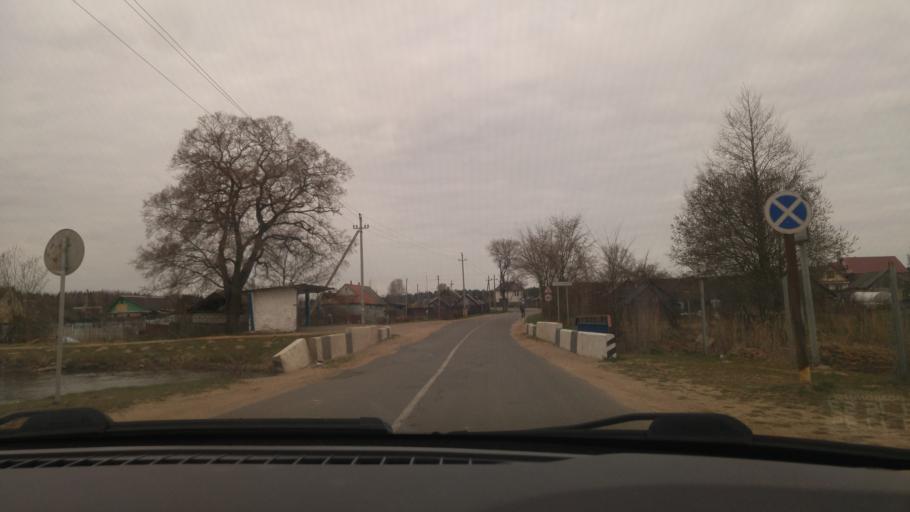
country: BY
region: Minsk
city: Smilavichy
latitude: 53.7150
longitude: 28.1404
